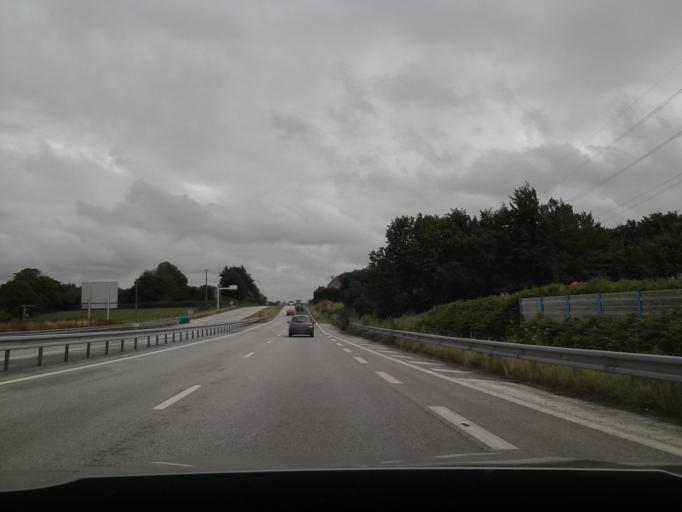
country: FR
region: Lower Normandy
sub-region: Departement de la Manche
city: La Glacerie
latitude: 49.5853
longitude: -1.5946
